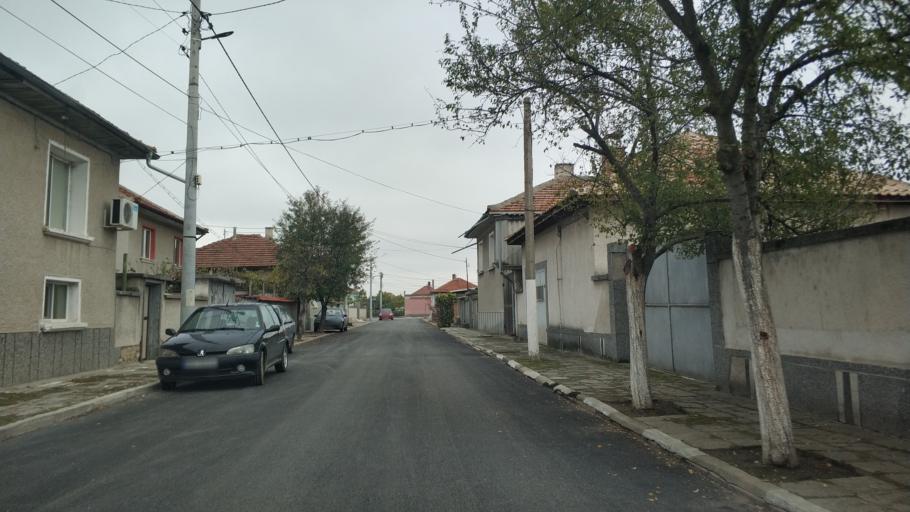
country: BG
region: Plovdiv
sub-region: Obshtina Kaloyanovo
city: Kaloyanovo
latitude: 42.3705
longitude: 24.7184
